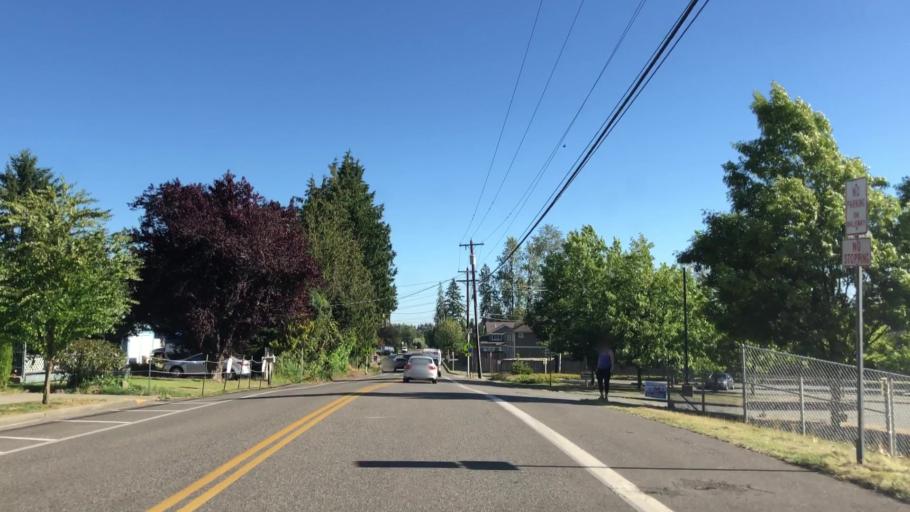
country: US
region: Washington
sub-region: Snohomish County
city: Martha Lake
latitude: 47.8580
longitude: -122.2579
